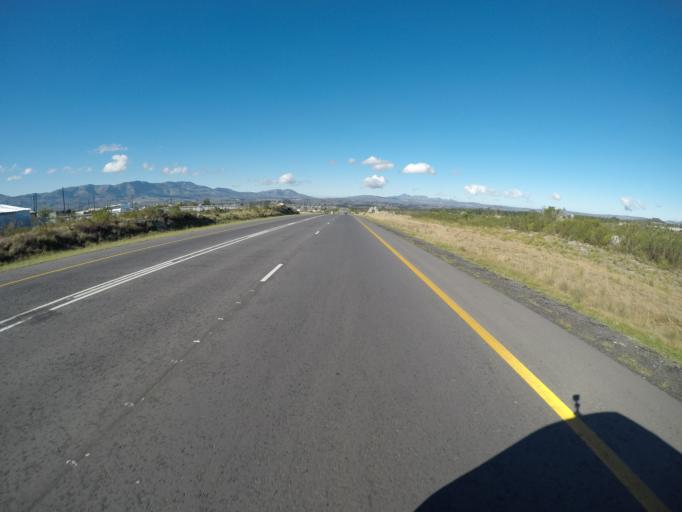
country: ZA
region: Western Cape
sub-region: Overberg District Municipality
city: Grabouw
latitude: -34.1601
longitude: 18.9780
